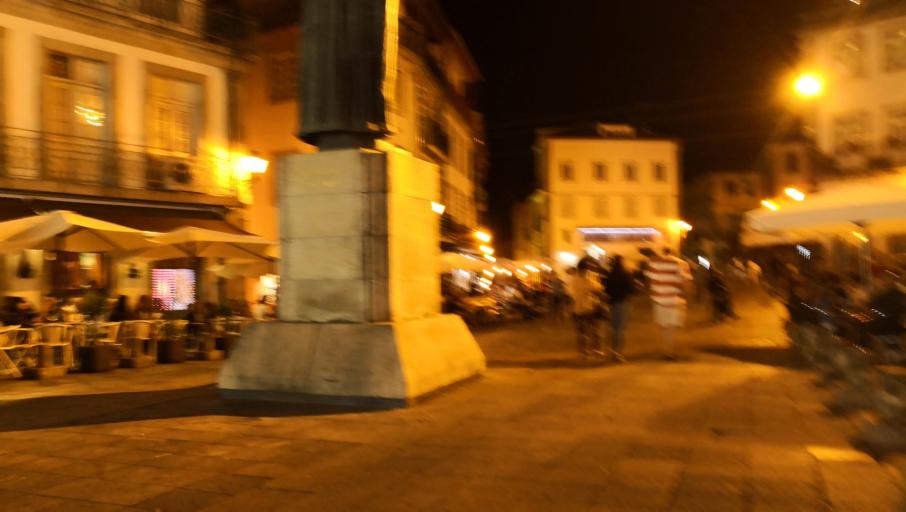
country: PT
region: Viseu
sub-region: Viseu
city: Viseu
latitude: 40.6596
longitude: -7.9116
